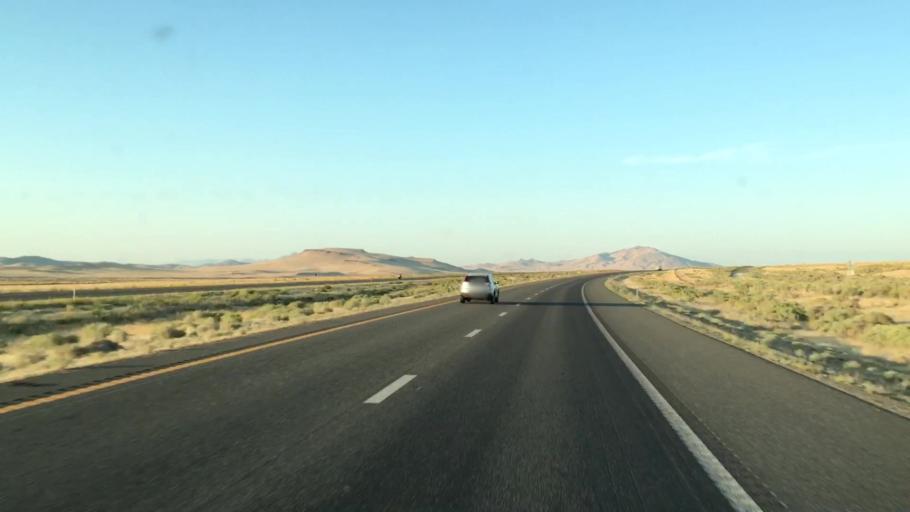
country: US
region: Nevada
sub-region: Humboldt County
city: Winnemucca
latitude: 40.8732
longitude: -117.9395
